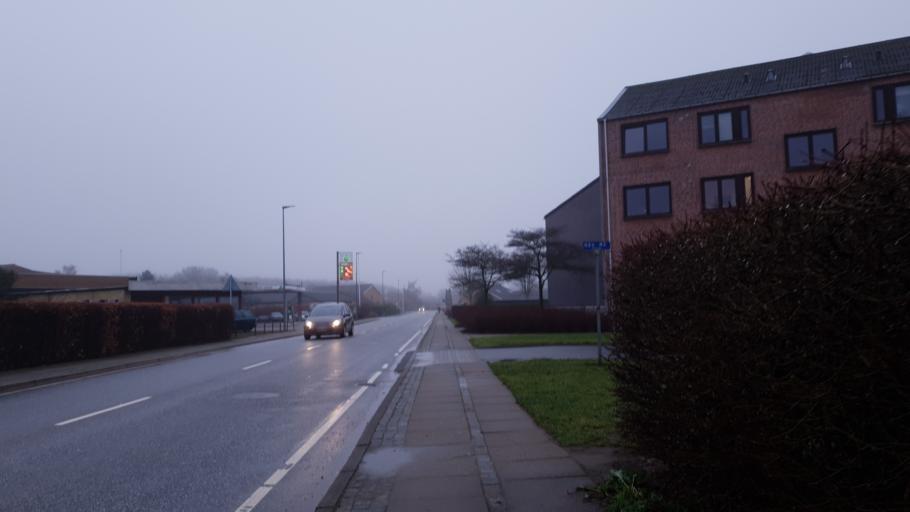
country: DK
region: Central Jutland
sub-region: Hedensted Kommune
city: Hedensted
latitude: 55.8001
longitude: 9.6962
